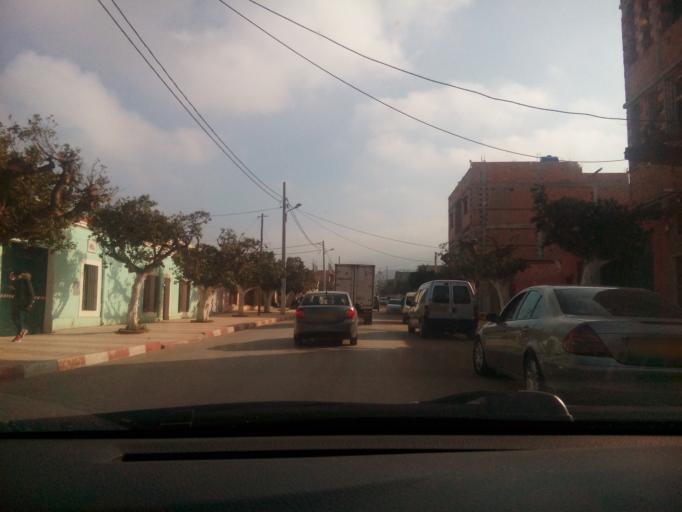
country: DZ
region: Oran
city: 'Ain el Turk
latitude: 35.7019
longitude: -0.8135
